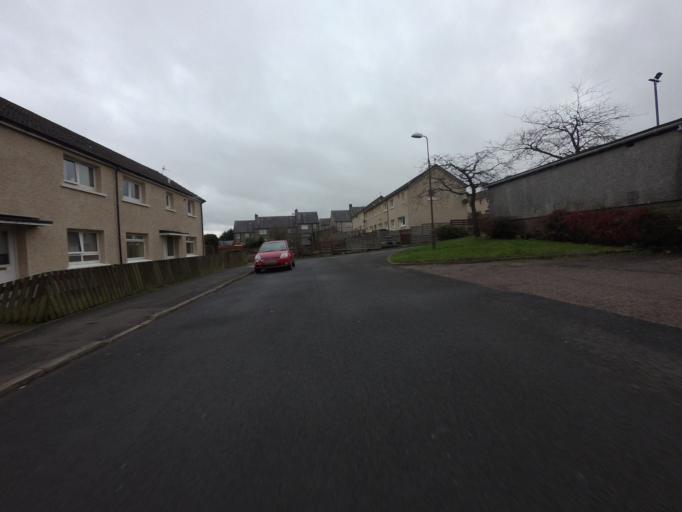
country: GB
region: Scotland
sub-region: West Lothian
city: Livingston
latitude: 55.9022
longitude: -3.5656
